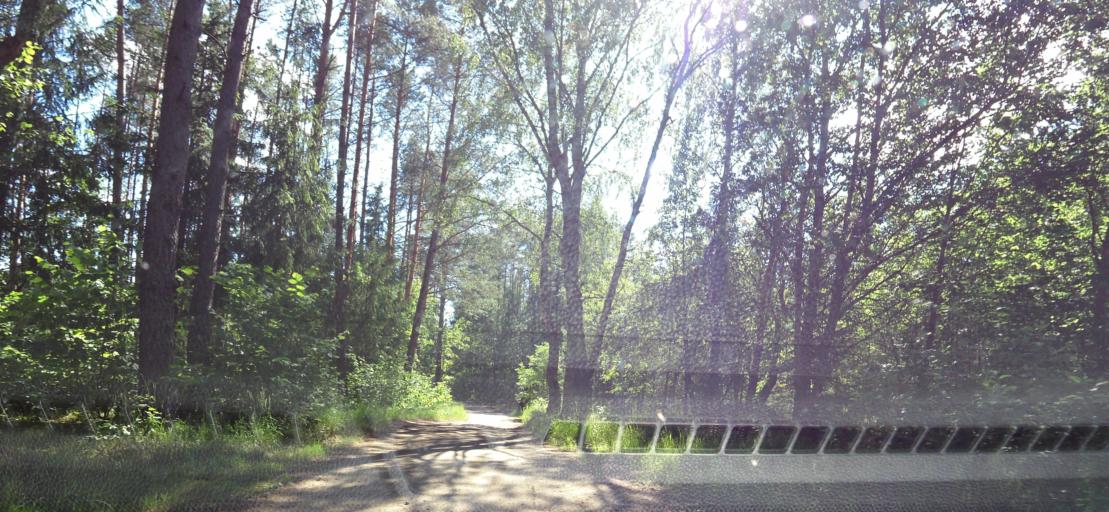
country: LT
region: Vilnius County
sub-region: Vilnius
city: Fabijoniskes
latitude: 54.8286
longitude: 25.3221
